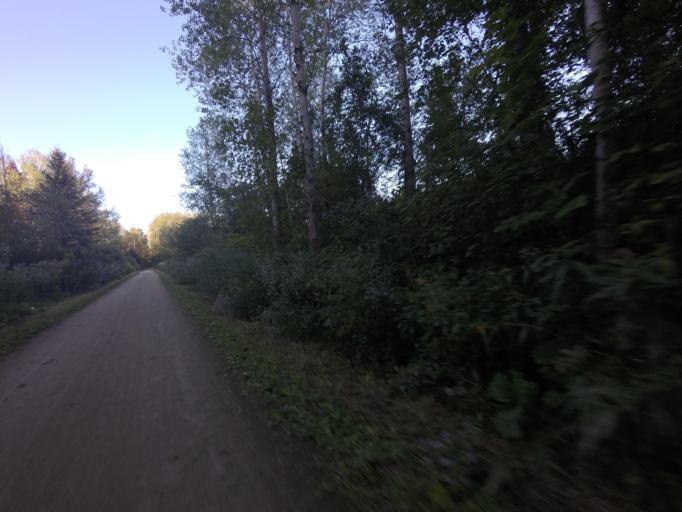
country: CA
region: Ontario
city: Brampton
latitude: 43.8531
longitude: -79.8771
